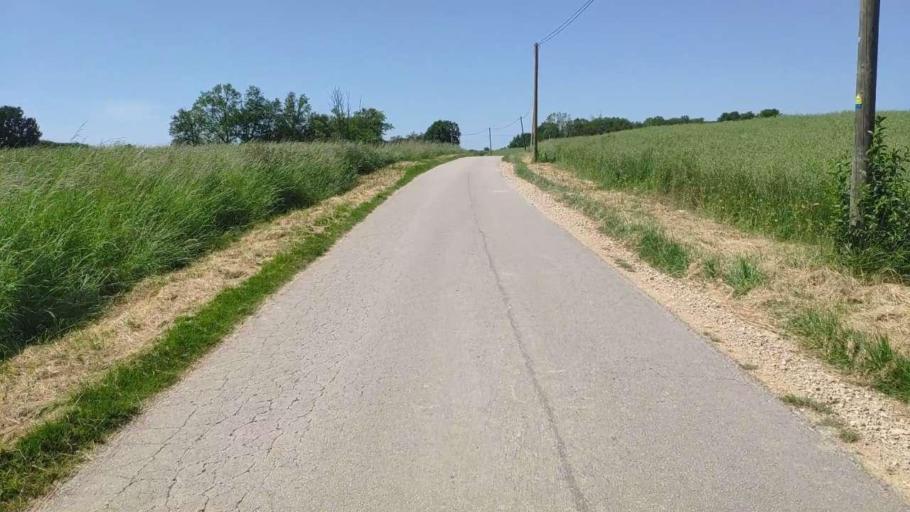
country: FR
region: Franche-Comte
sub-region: Departement du Jura
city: Bletterans
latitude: 46.7705
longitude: 5.4072
